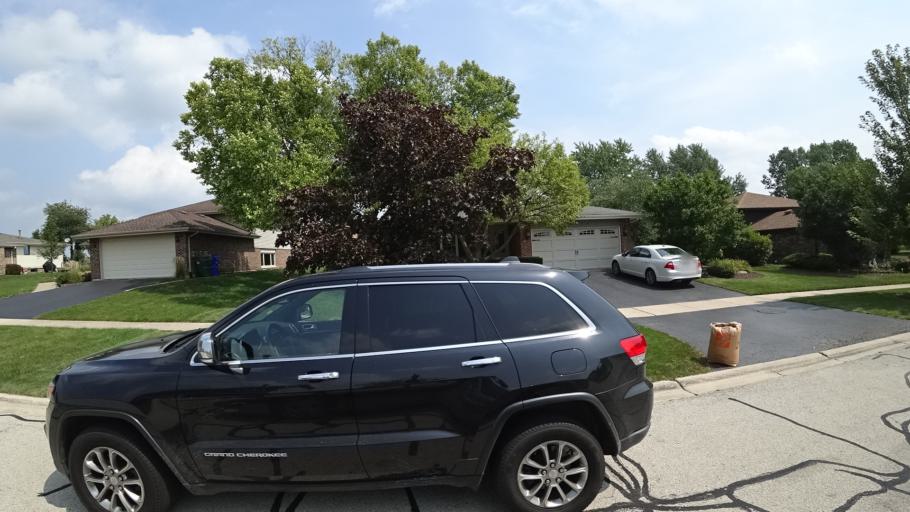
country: US
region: Illinois
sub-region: Will County
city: Goodings Grove
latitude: 41.6242
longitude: -87.8976
